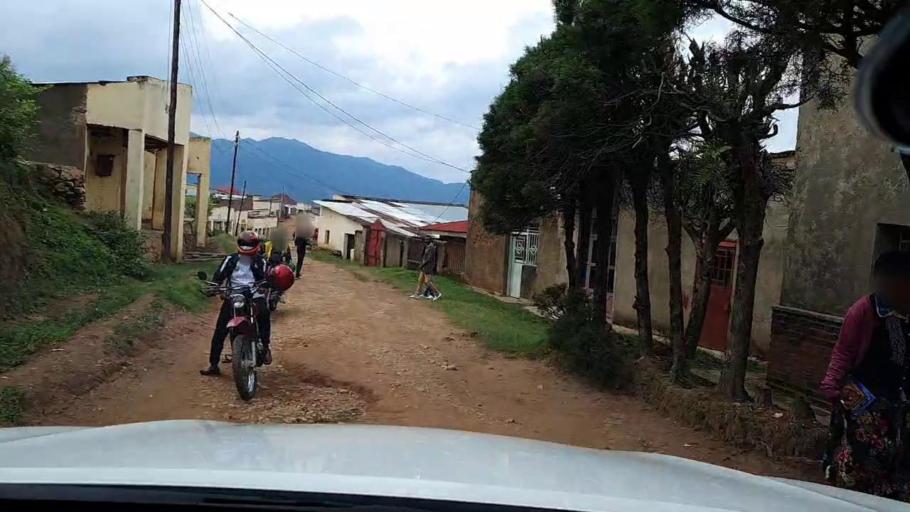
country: RW
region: Western Province
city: Kibuye
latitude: -2.1835
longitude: 29.2935
